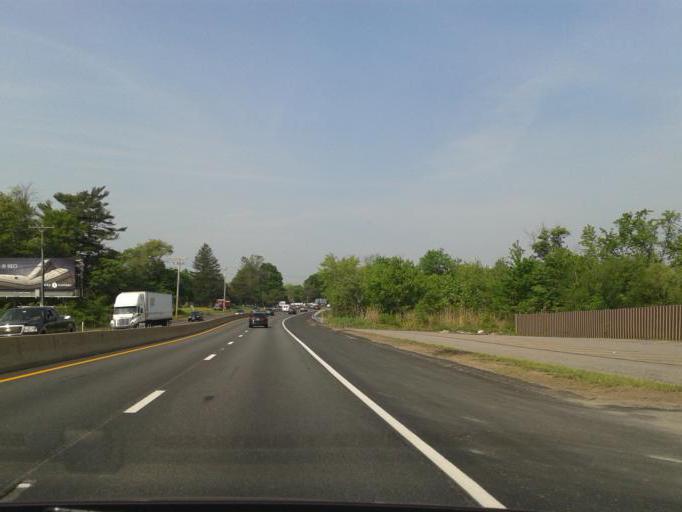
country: US
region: Massachusetts
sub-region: Worcester County
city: Westborough
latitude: 42.2857
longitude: -71.5993
